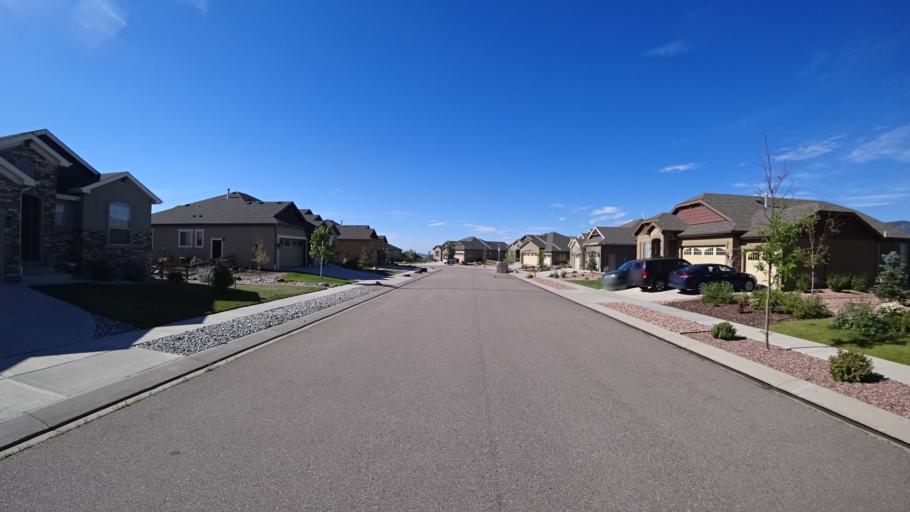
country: US
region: Colorado
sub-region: El Paso County
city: Gleneagle
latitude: 39.0333
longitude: -104.8260
